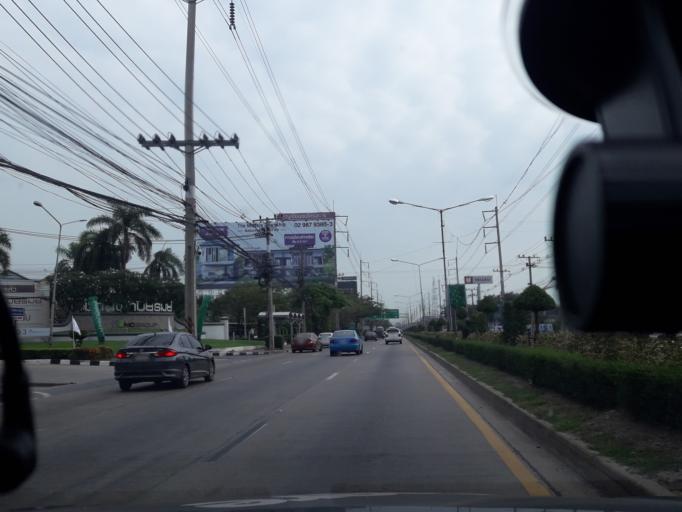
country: TH
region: Pathum Thani
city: Lam Luk Ka
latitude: 13.9346
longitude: 100.7395
